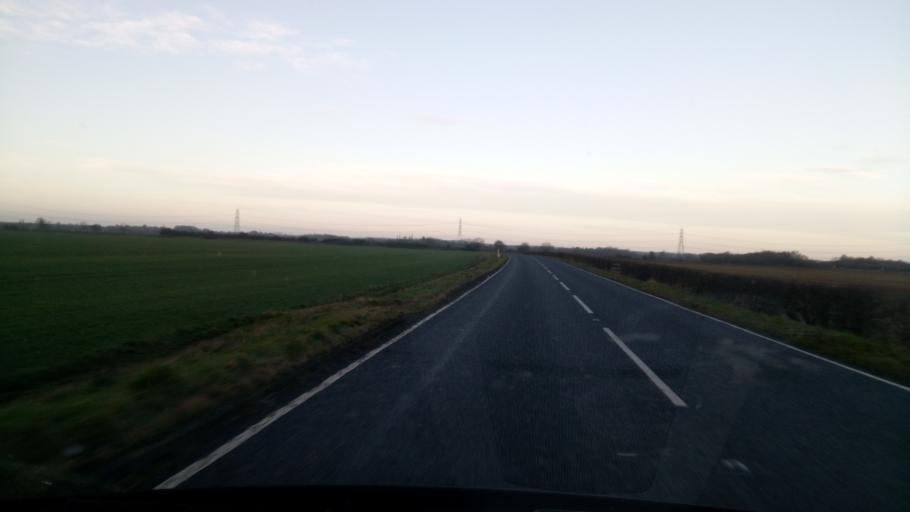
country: GB
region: England
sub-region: Peterborough
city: Castor
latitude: 52.5763
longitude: -0.3592
